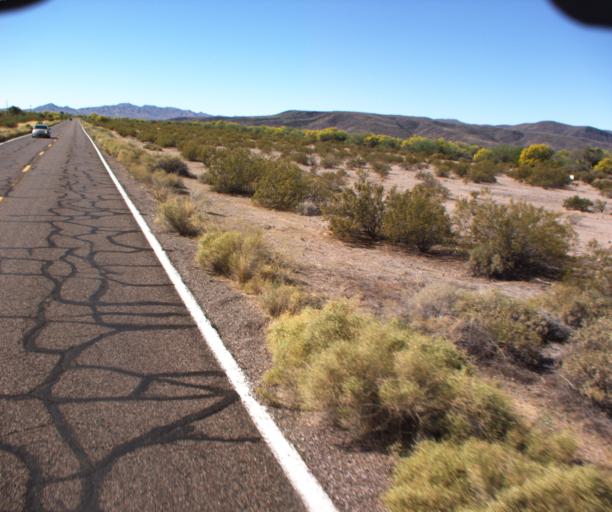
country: US
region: Arizona
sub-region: Pima County
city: Ajo
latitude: 32.5096
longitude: -112.8809
